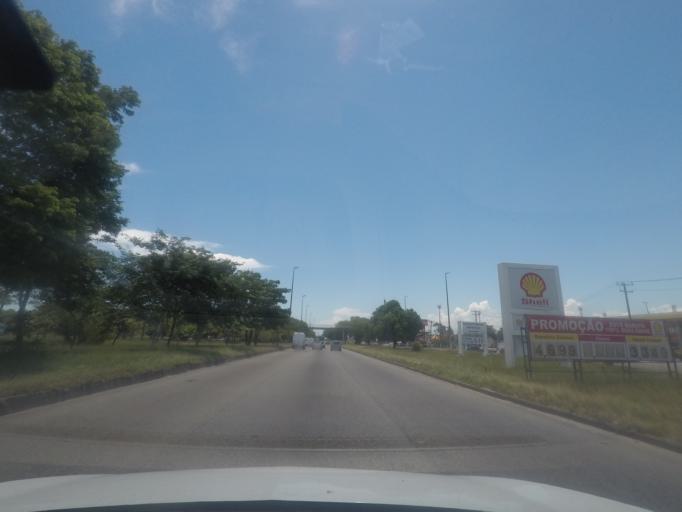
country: BR
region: Rio de Janeiro
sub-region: Itaguai
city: Itaguai
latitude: -22.8927
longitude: -43.6728
